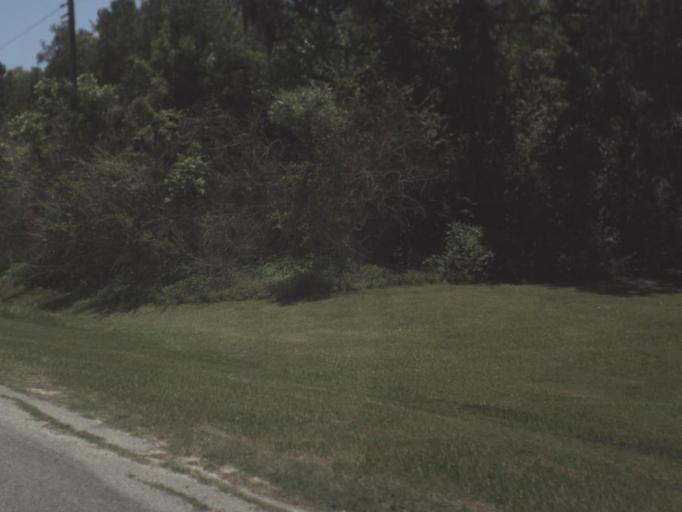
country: US
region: Florida
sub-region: Suwannee County
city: Live Oak
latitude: 30.3187
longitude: -83.0353
